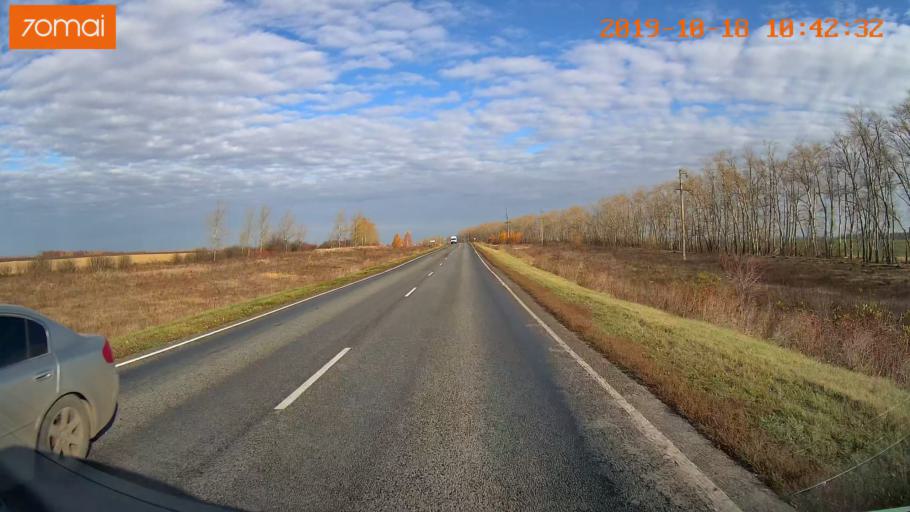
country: RU
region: Tula
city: Kurkino
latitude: 53.6248
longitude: 38.6806
